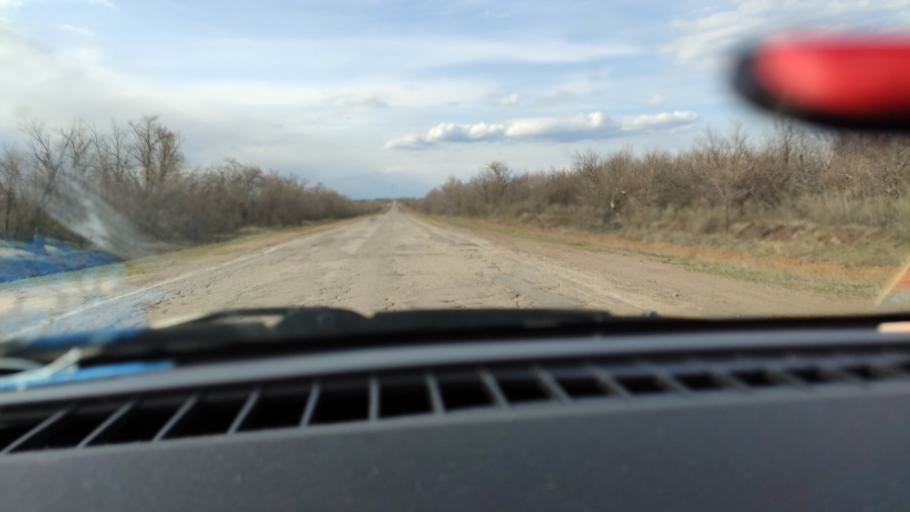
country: RU
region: Saratov
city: Rovnoye
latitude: 51.0015
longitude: 46.1038
